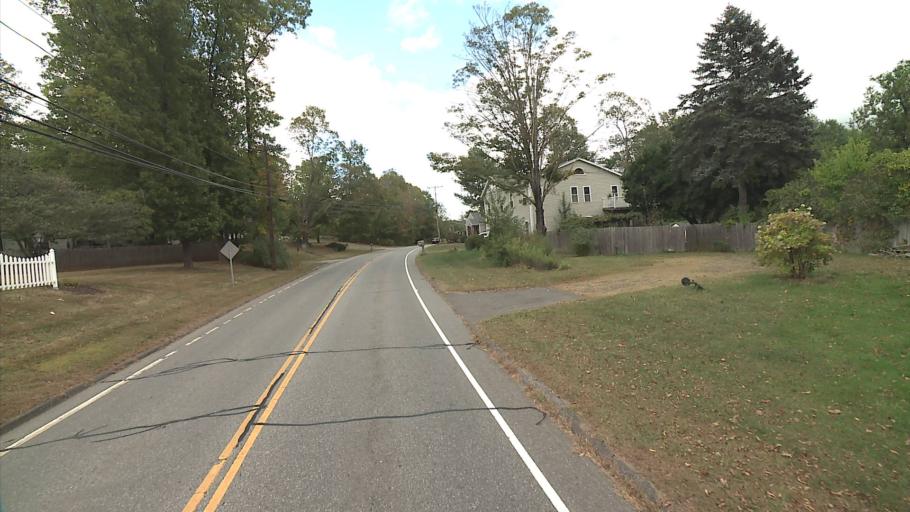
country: US
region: Connecticut
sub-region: Middlesex County
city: Durham
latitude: 41.5112
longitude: -72.7141
